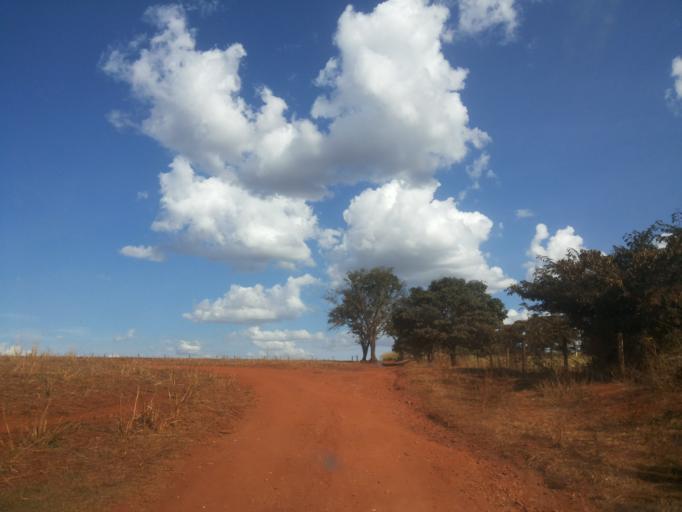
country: BR
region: Minas Gerais
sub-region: Capinopolis
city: Capinopolis
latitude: -18.5850
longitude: -49.4952
